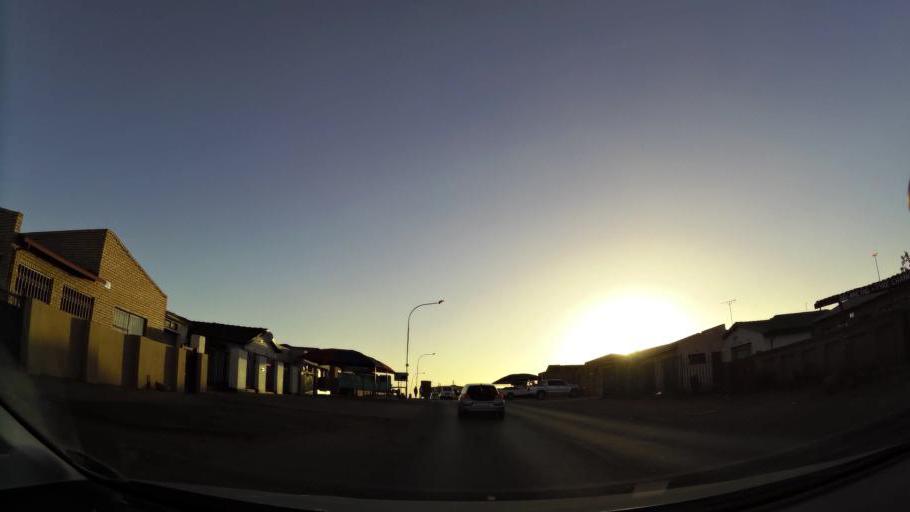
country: ZA
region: Gauteng
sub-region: Ekurhuleni Metropolitan Municipality
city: Tembisa
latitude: -25.9952
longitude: 28.2262
